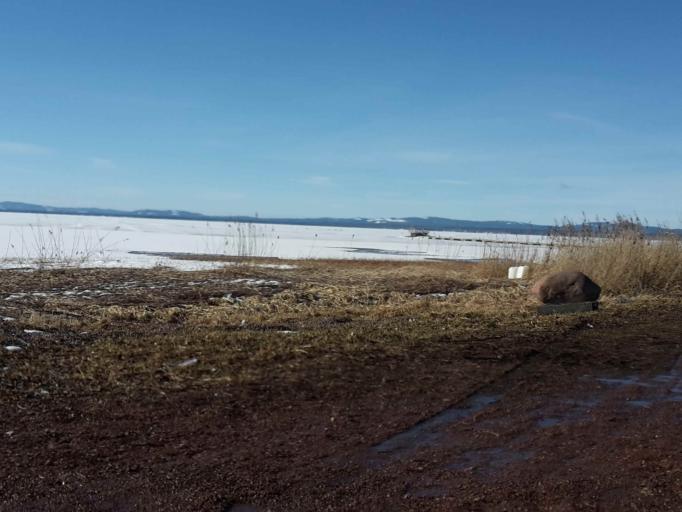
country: SE
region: Dalarna
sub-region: Orsa Kommun
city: Orsa
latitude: 61.1191
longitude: 14.6004
